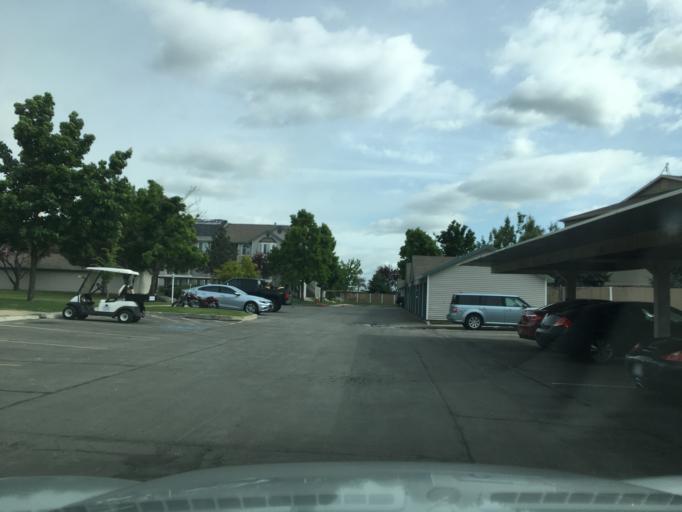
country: US
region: Utah
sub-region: Davis County
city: Layton
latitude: 41.0834
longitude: -111.9905
